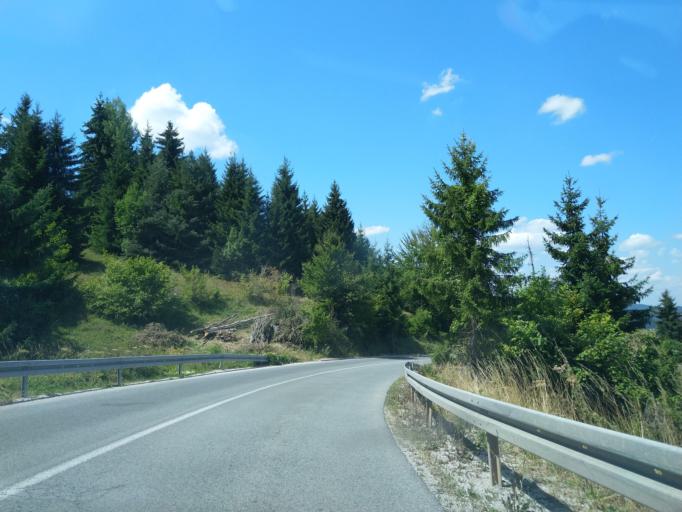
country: RS
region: Central Serbia
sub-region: Zlatiborski Okrug
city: Nova Varos
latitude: 43.4073
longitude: 19.8404
